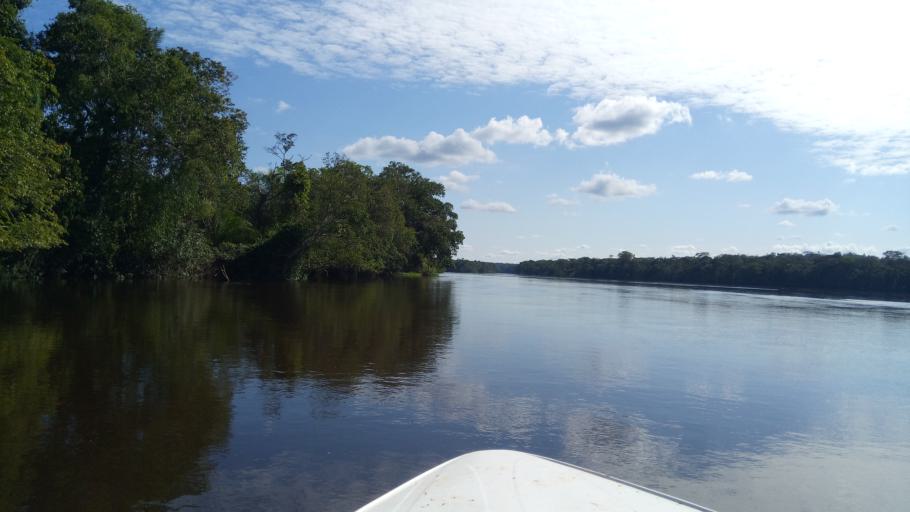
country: CD
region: Eastern Province
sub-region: Sous-Region de la Tshopo
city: Yangambi
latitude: 0.5334
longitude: 24.1987
